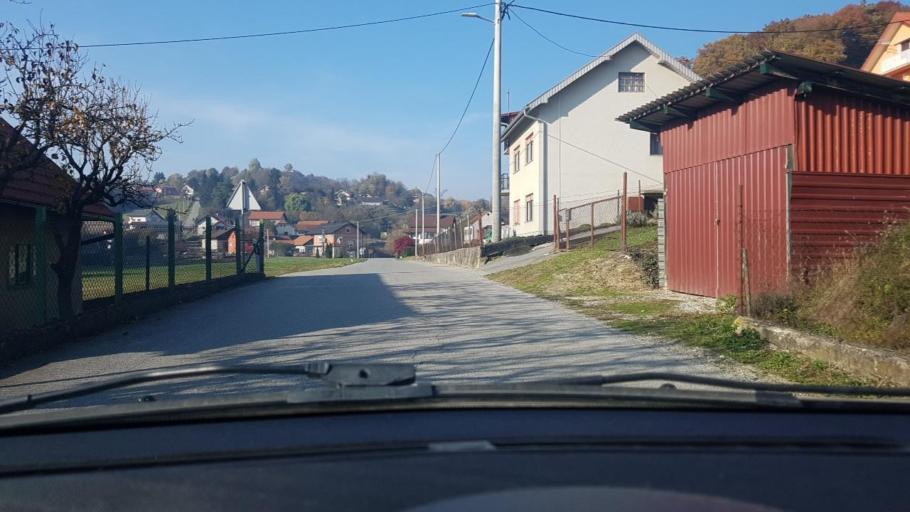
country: HR
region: Krapinsko-Zagorska
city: Zabok
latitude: 46.0295
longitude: 15.8846
